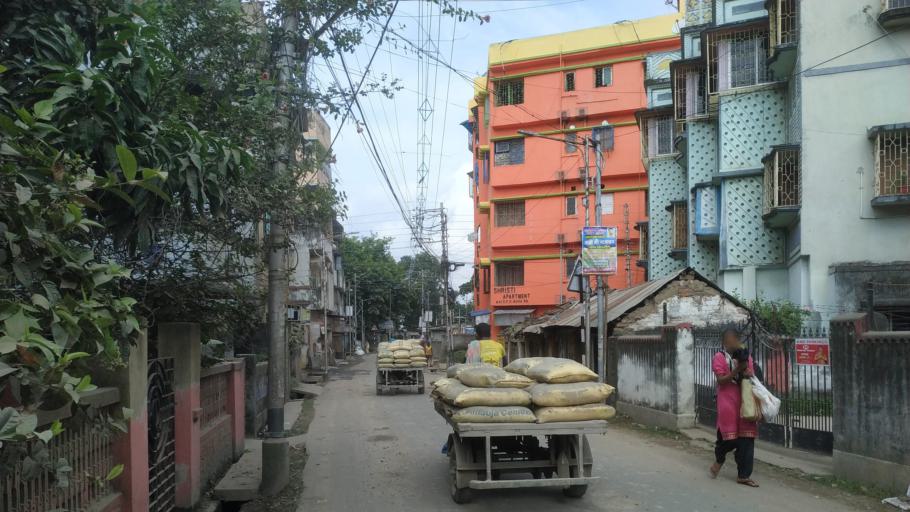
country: IN
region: West Bengal
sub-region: North 24 Parganas
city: Dam Dam
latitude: 22.6401
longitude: 88.4151
